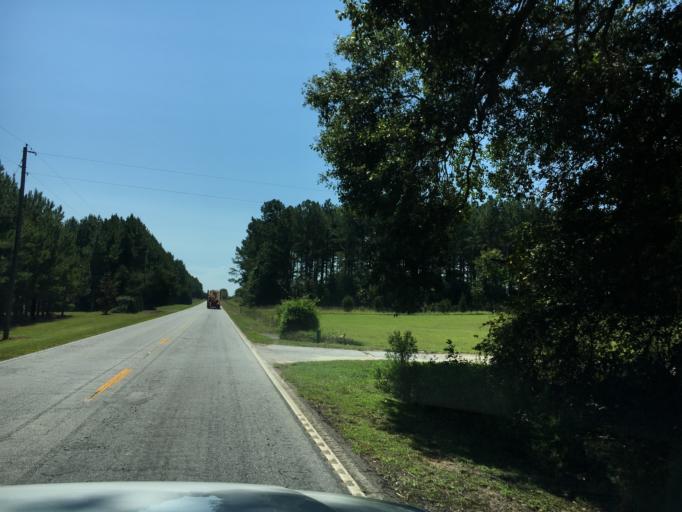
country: US
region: South Carolina
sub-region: Laurens County
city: Joanna
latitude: 34.4080
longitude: -81.8602
